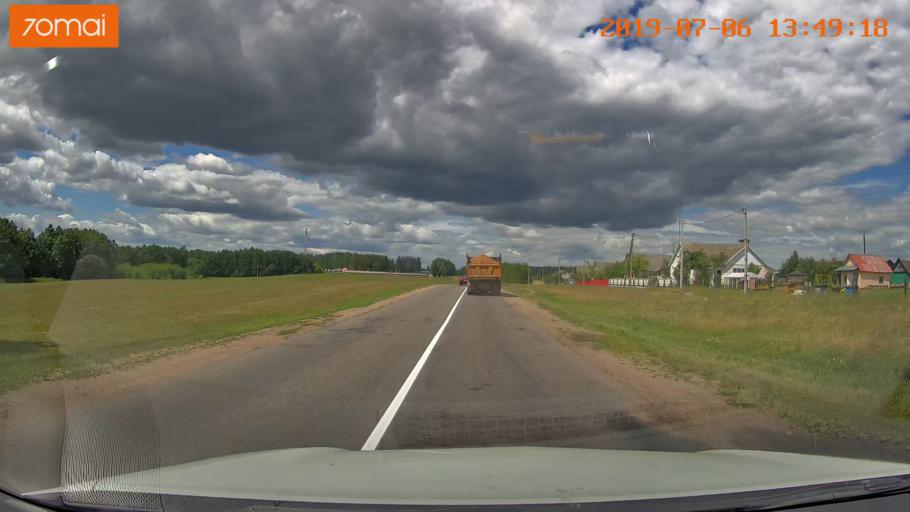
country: BY
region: Minsk
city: Ivyanyets
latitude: 53.6932
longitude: 26.8527
